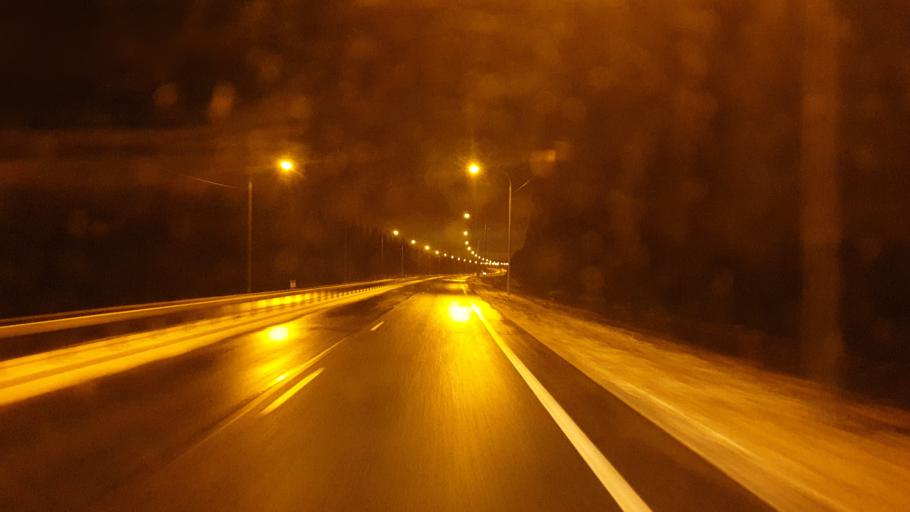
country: FI
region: Northern Savo
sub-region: Kuopio
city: Kuopio
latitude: 62.7677
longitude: 27.5827
